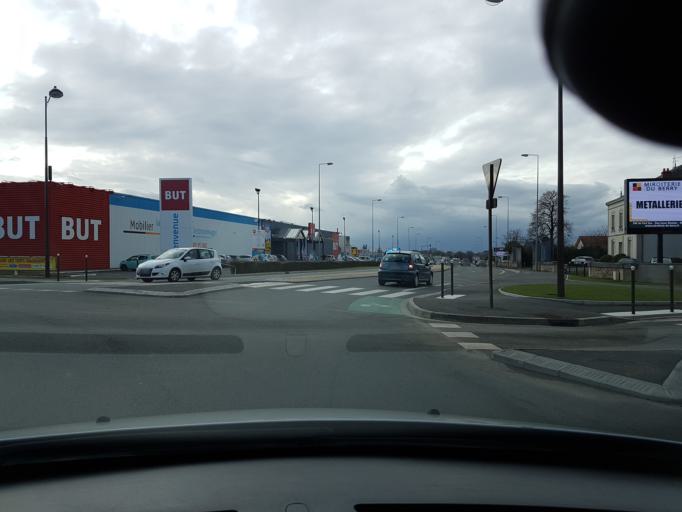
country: FR
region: Centre
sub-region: Departement du Cher
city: Bourges
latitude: 47.0958
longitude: 2.4354
